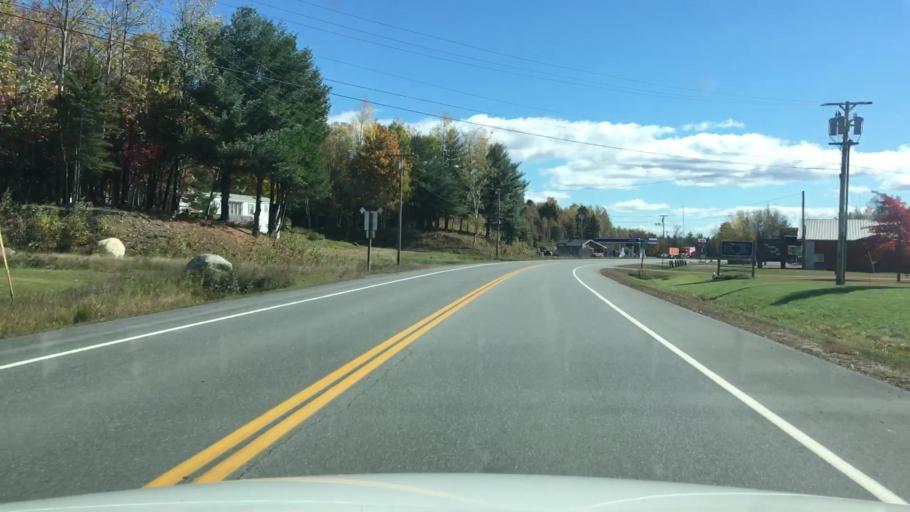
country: US
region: Maine
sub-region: Penobscot County
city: Medway
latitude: 45.6112
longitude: -68.5266
